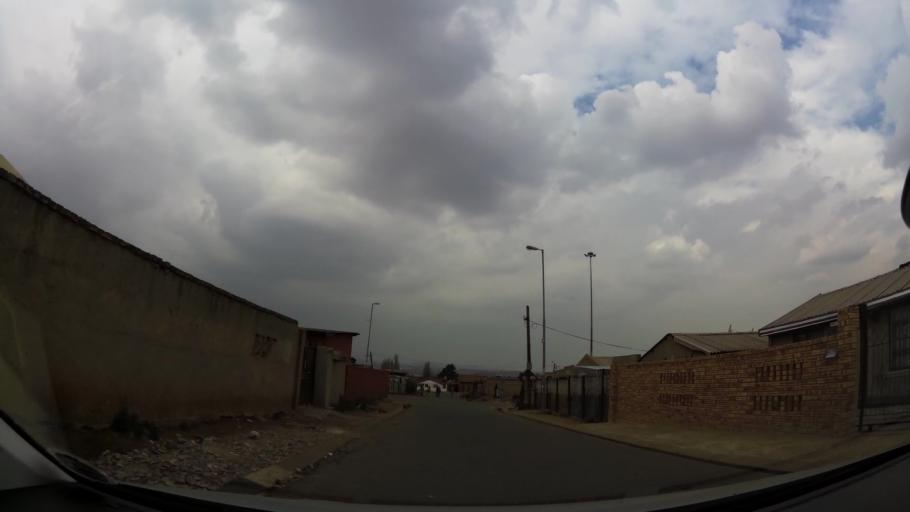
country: ZA
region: Gauteng
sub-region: City of Johannesburg Metropolitan Municipality
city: Soweto
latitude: -26.2615
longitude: 27.8630
